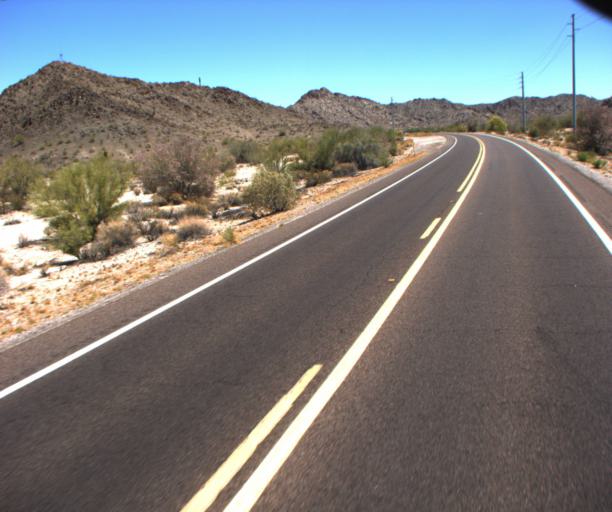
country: US
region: Arizona
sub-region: La Paz County
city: Salome
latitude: 33.7246
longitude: -113.6892
